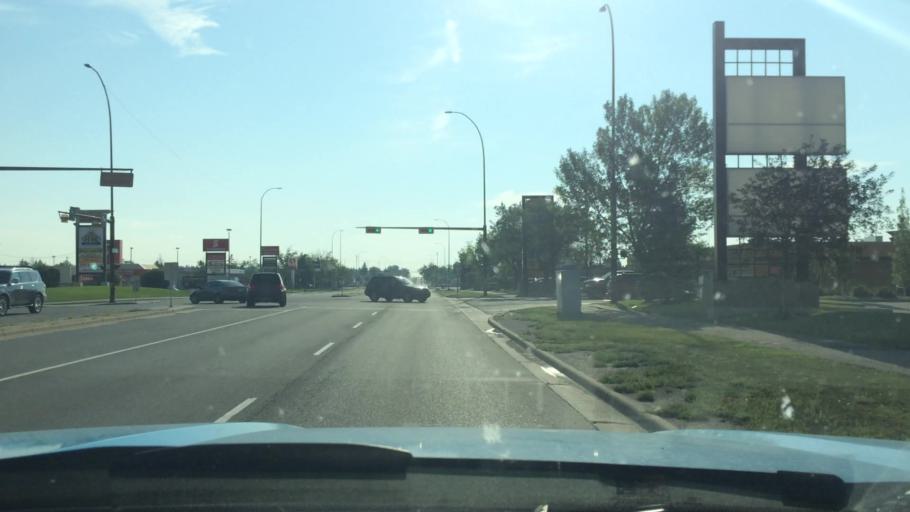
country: CA
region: Alberta
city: Calgary
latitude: 51.0814
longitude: -113.9863
